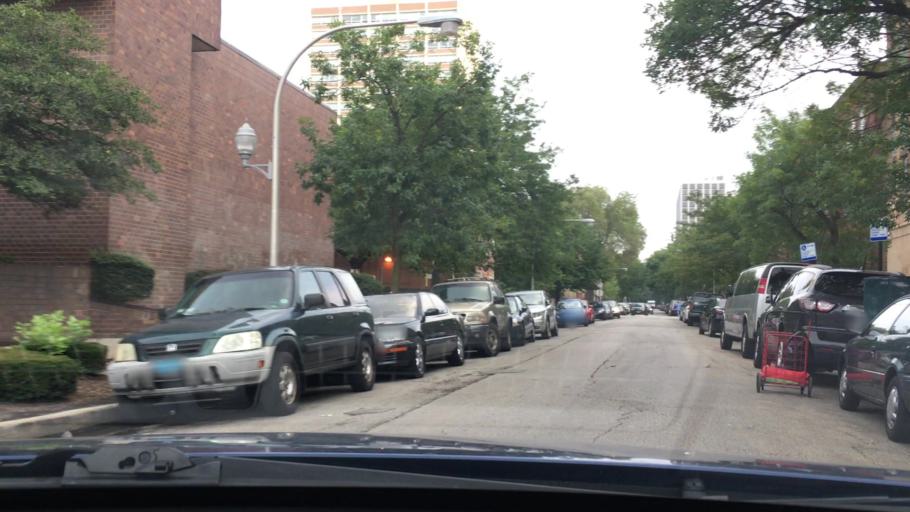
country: US
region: Illinois
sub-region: Cook County
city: Evanston
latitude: 41.9653
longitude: -87.6524
